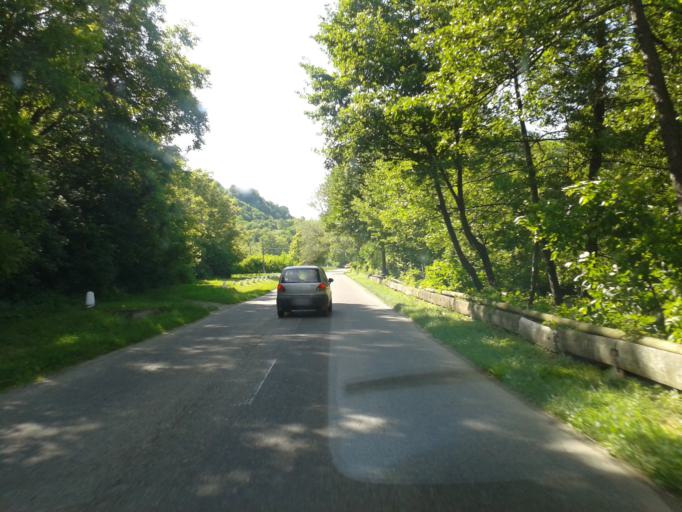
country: RO
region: Hunedoara
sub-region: Comuna Geoagiu
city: Geoagiu
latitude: 45.9351
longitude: 23.1909
